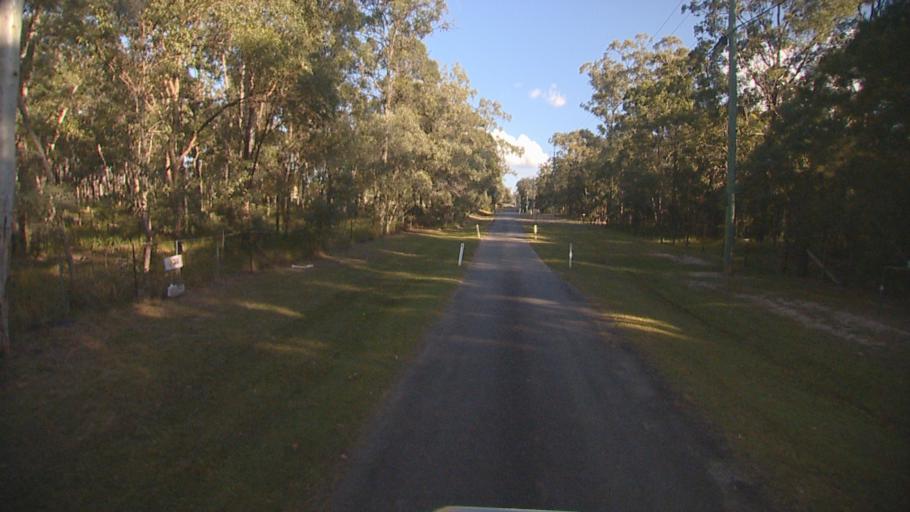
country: AU
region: Queensland
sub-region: Gold Coast
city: Yatala
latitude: -27.6671
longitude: 153.2447
